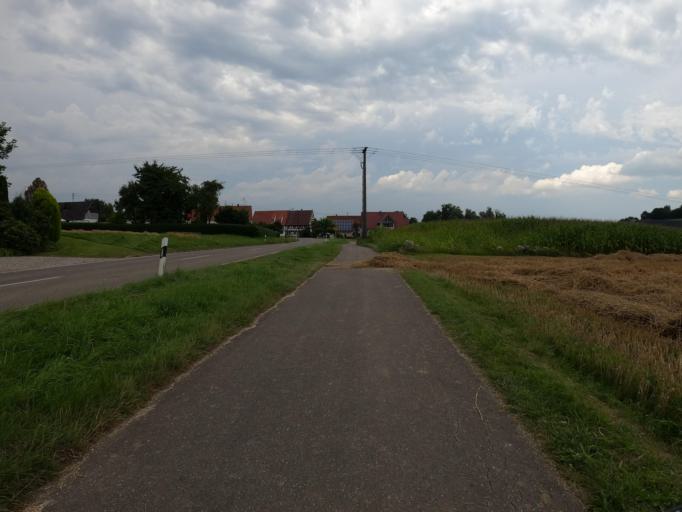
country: DE
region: Bavaria
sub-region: Swabia
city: Pfaffenhofen an der Roth
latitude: 48.3978
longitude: 10.1876
